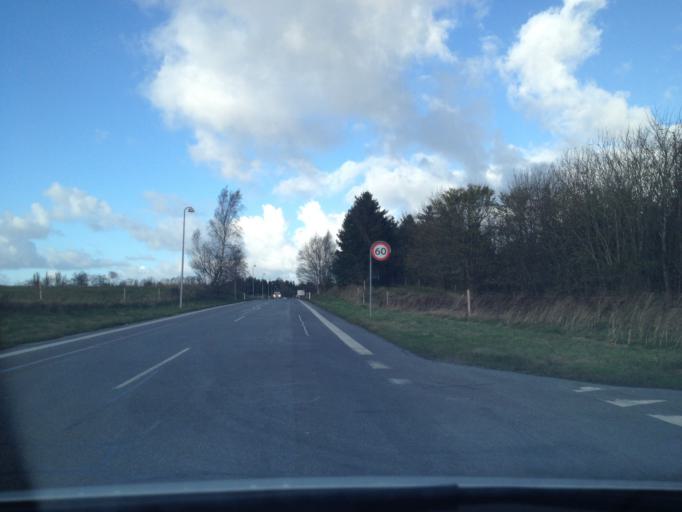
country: DK
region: Capital Region
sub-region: Fureso Kommune
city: Farum
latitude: 55.8315
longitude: 12.3746
